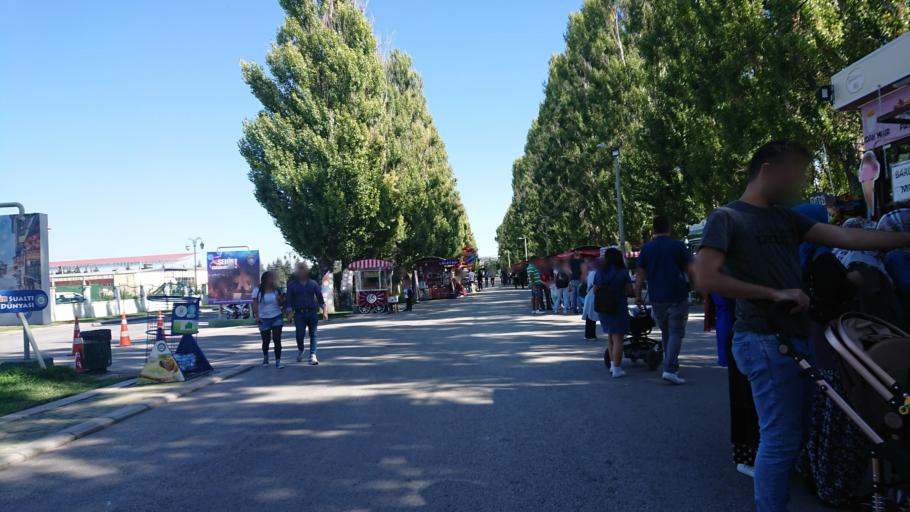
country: TR
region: Eskisehir
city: Eskisehir
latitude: 39.7645
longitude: 30.4744
